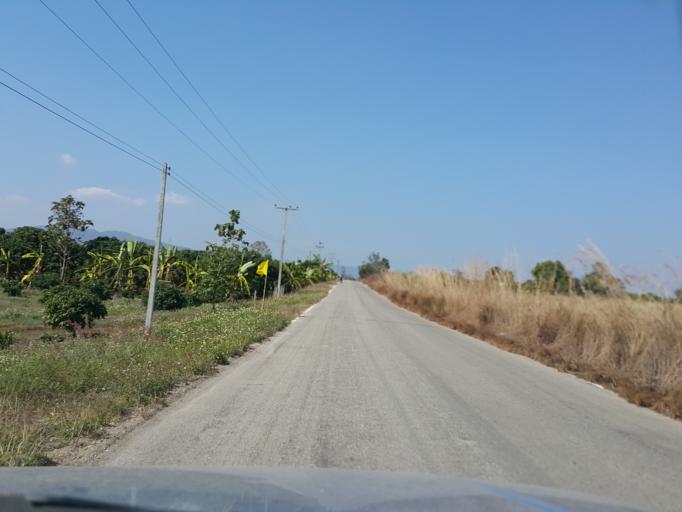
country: TH
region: Chiang Mai
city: Mae Wang
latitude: 18.5616
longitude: 98.7933
